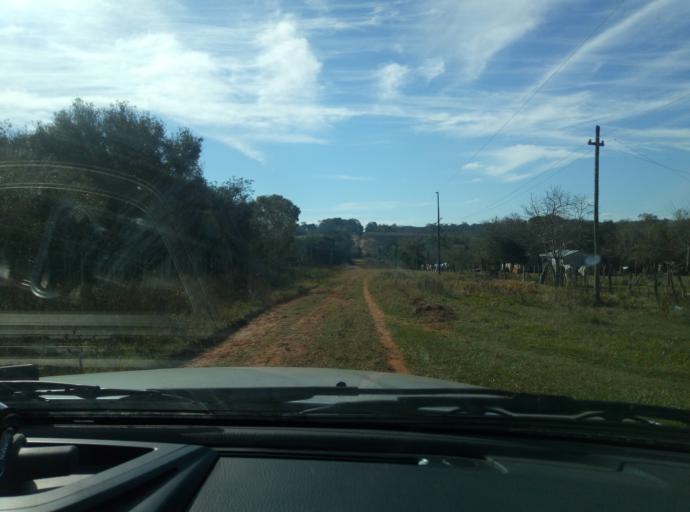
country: PY
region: Caaguazu
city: Carayao
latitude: -25.1688
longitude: -56.2931
